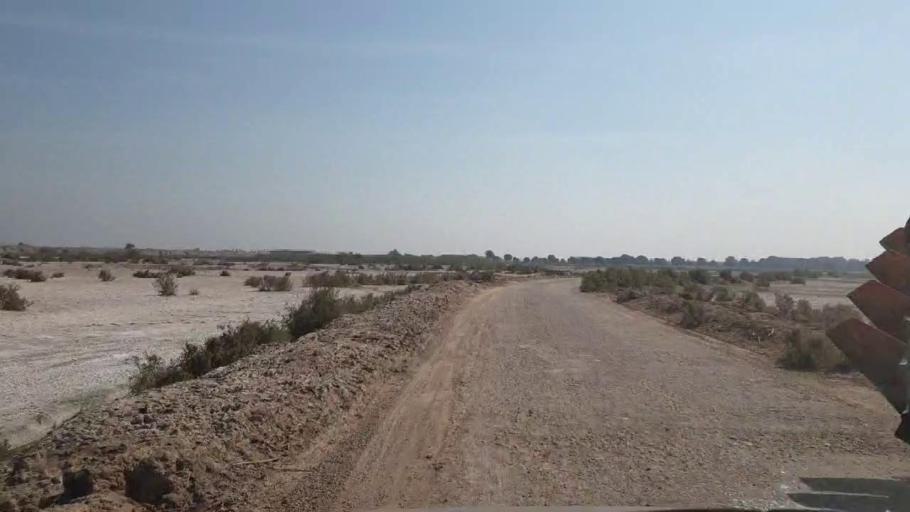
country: PK
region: Sindh
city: Chambar
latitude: 25.3841
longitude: 68.8023
